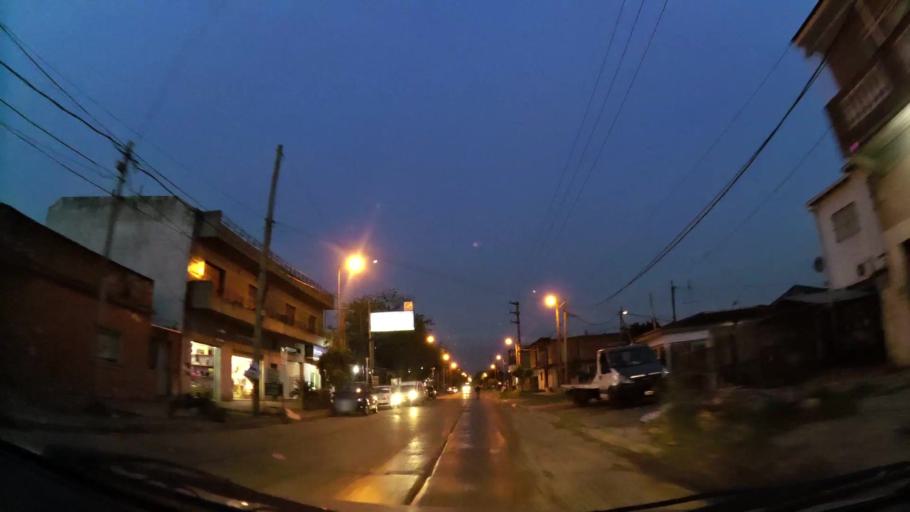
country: AR
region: Buenos Aires
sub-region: Partido de Lomas de Zamora
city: Lomas de Zamora
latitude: -34.7428
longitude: -58.3614
